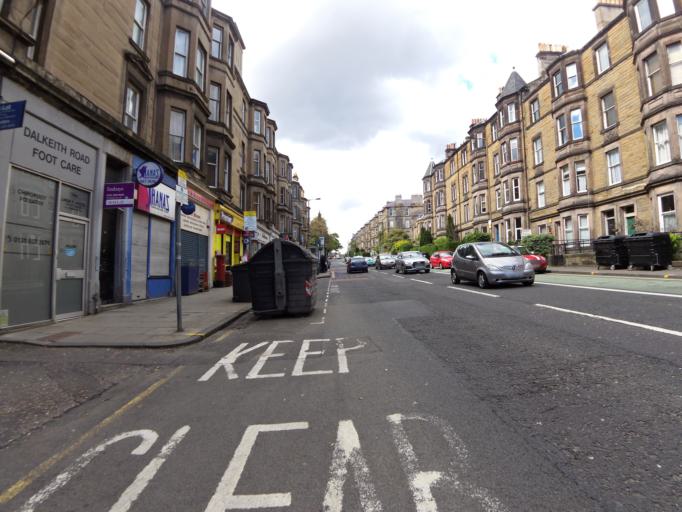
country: GB
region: Scotland
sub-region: Edinburgh
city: Edinburgh
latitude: 55.9333
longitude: -3.1662
